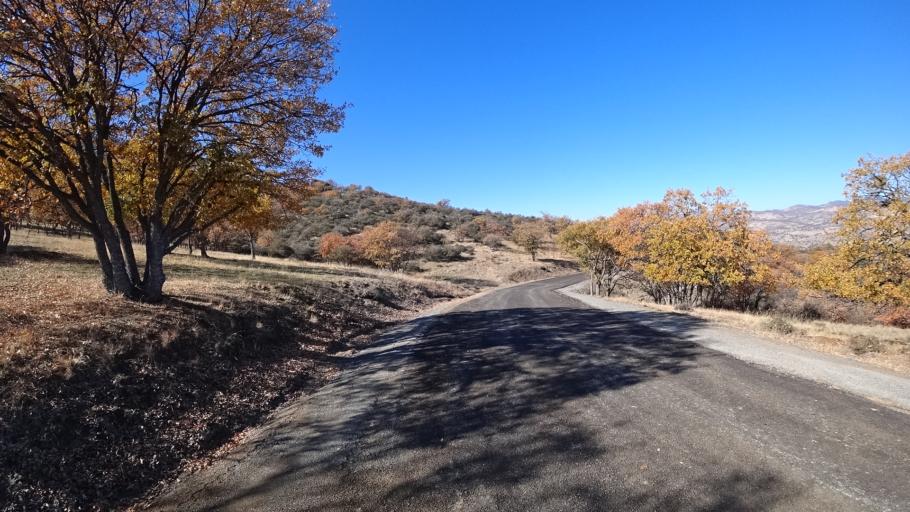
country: US
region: California
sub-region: Siskiyou County
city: Montague
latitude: 41.8756
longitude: -122.4882
